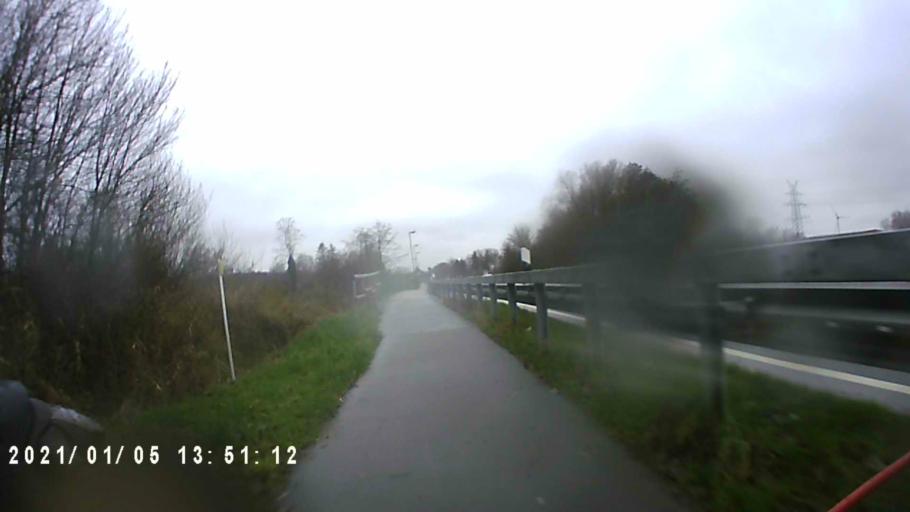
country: DE
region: Lower Saxony
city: Weener
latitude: 53.1729
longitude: 7.3624
